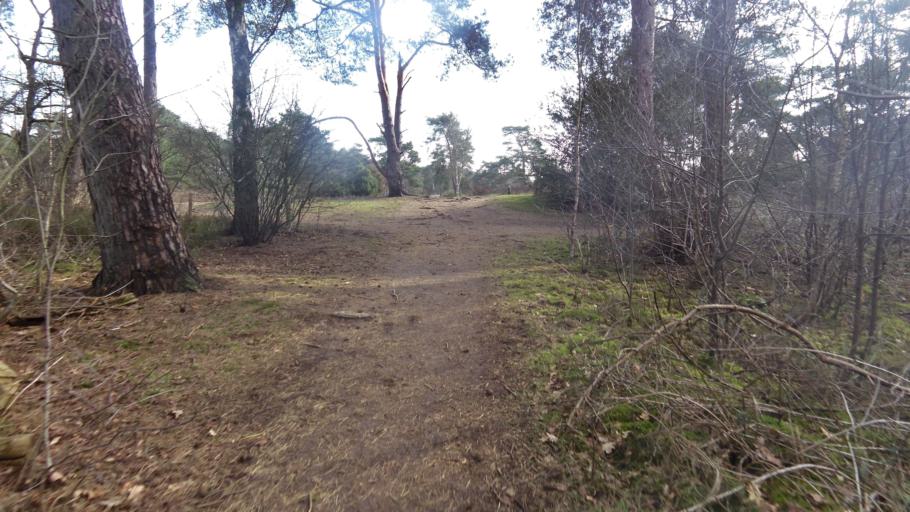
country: NL
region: Utrecht
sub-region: Gemeente Utrechtse Heuvelrug
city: Maarn
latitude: 52.0700
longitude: 5.3651
